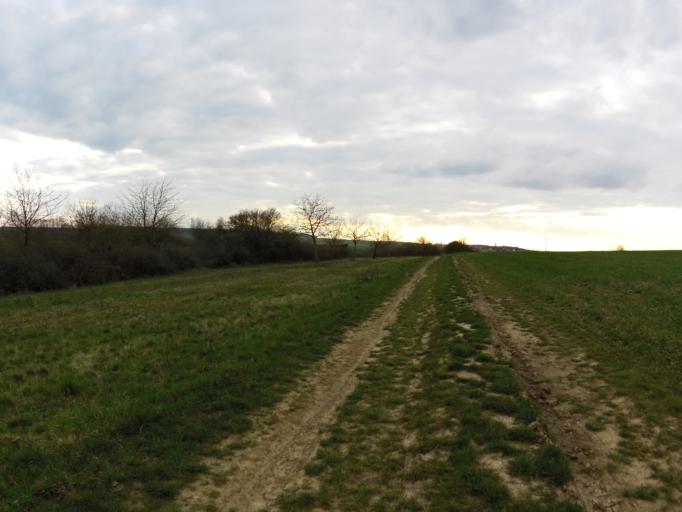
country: DE
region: Bavaria
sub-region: Regierungsbezirk Unterfranken
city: Biebelried
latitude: 49.7450
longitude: 10.0951
